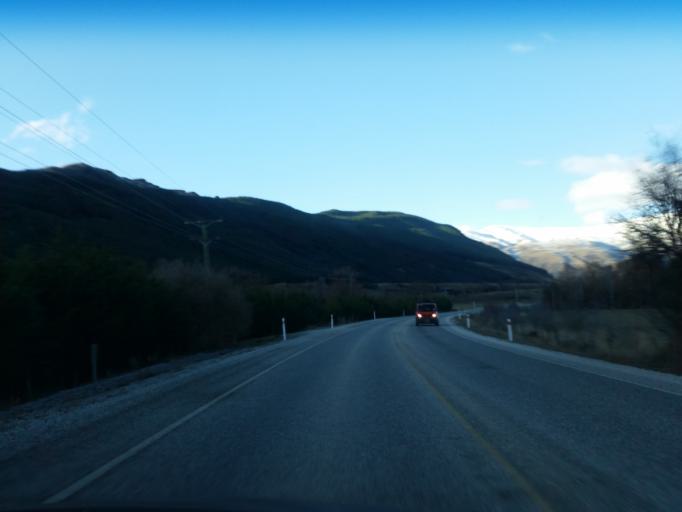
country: NZ
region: Otago
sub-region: Queenstown-Lakes District
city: Arrowtown
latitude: -44.9469
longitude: 168.7669
